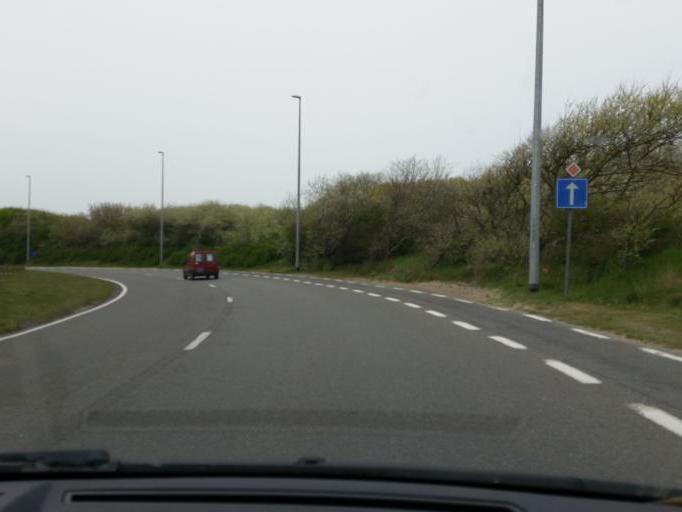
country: BE
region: Flanders
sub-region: Provincie West-Vlaanderen
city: Wenduine
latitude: 51.2975
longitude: 3.0738
